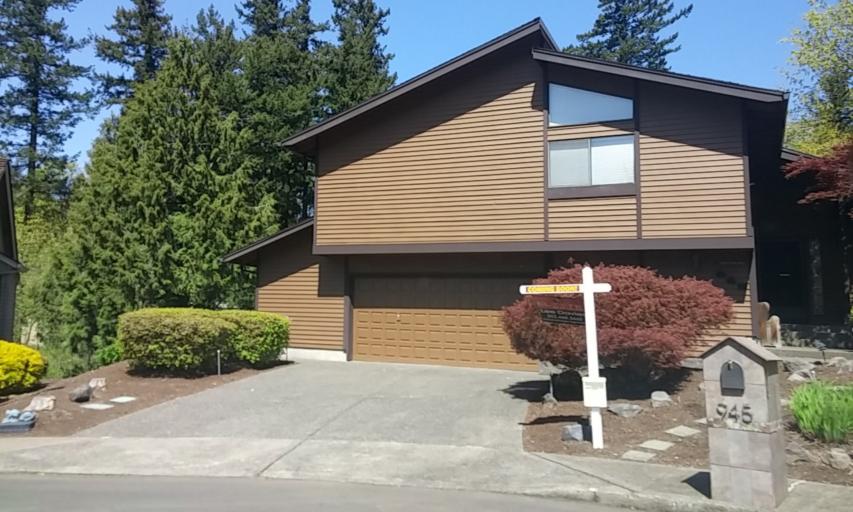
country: US
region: Oregon
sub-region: Washington County
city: West Haven
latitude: 45.5263
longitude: -122.7680
